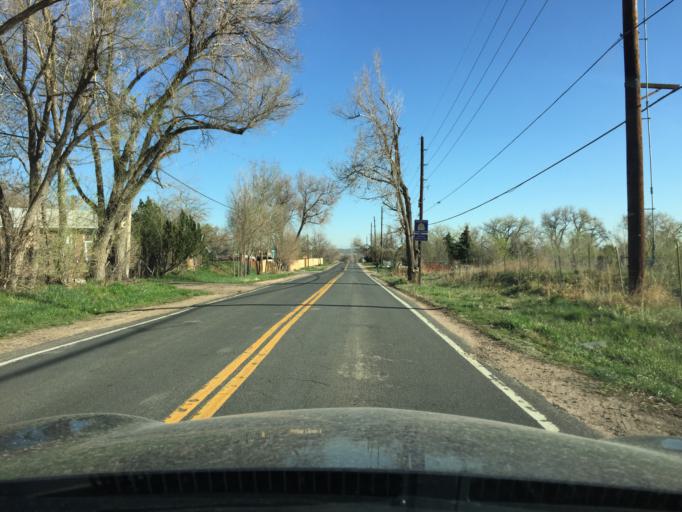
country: US
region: Colorado
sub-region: Boulder County
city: Erie
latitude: 40.0441
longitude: -105.0745
